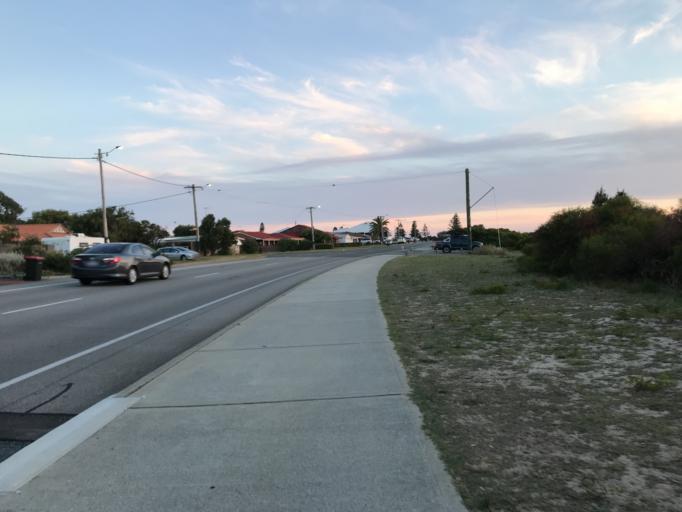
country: AU
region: Western Australia
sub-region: Rockingham
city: Shoalwater
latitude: -32.3014
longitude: 115.7038
